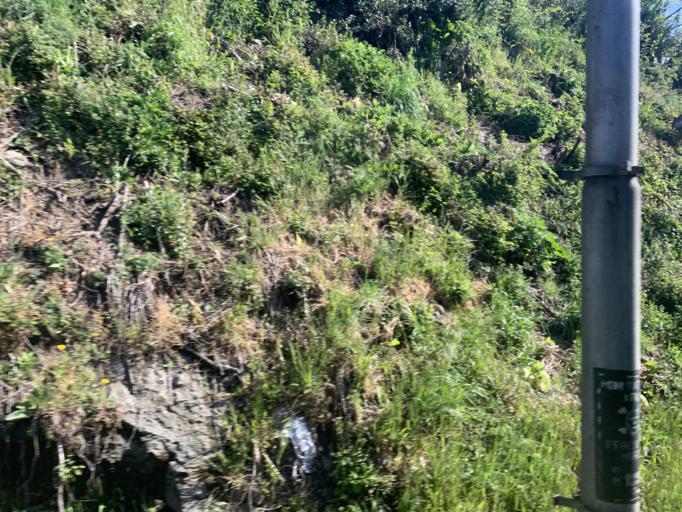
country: IT
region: Latium
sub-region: Citta metropolitana di Roma Capitale
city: Castel Gandolfo
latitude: 41.7694
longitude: 12.6508
